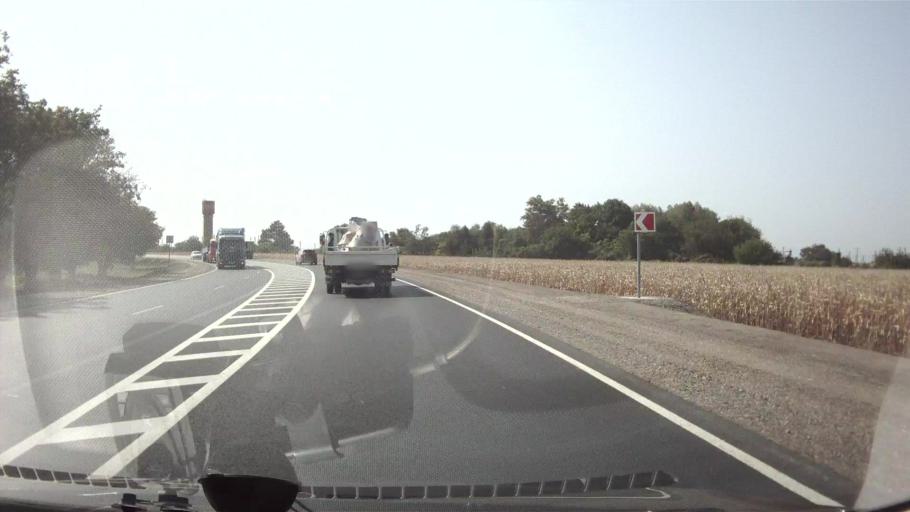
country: RU
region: Krasnodarskiy
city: Ust'-Labinsk
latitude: 45.2438
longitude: 39.6516
